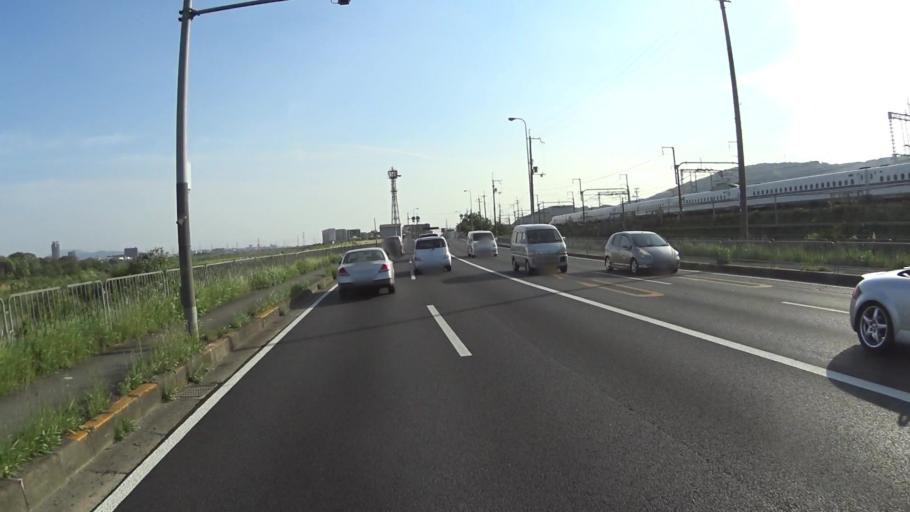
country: JP
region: Kyoto
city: Yawata
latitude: 34.8878
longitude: 135.6781
